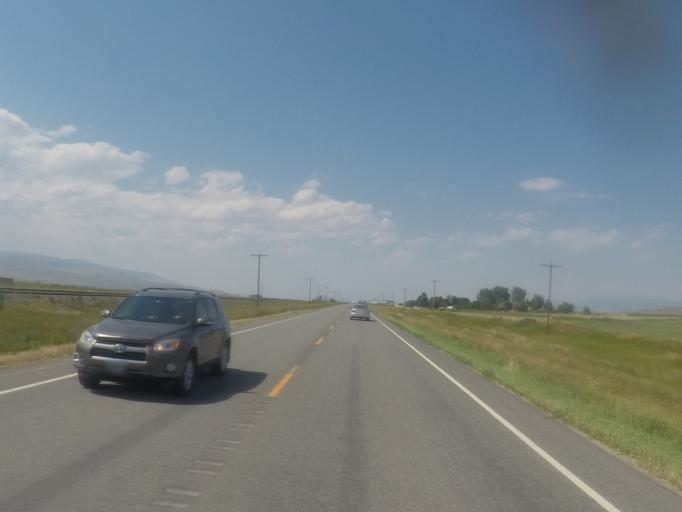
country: US
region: Montana
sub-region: Broadwater County
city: Townsend
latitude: 46.1844
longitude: -111.4461
